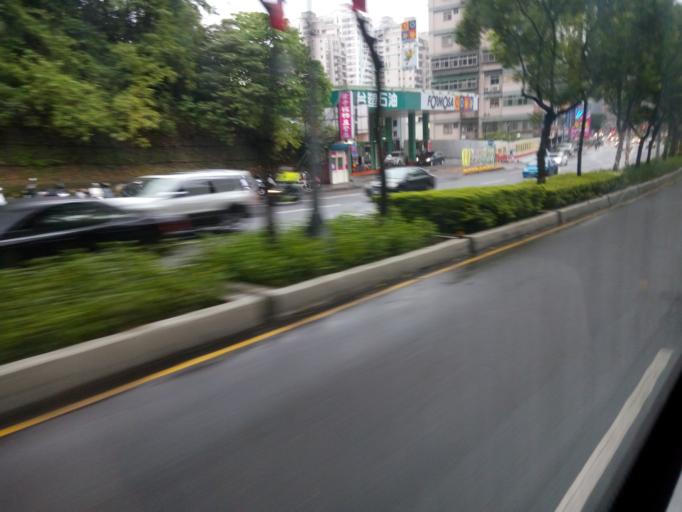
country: TW
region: Taiwan
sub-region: Keelung
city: Keelung
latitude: 25.0615
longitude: 121.6508
